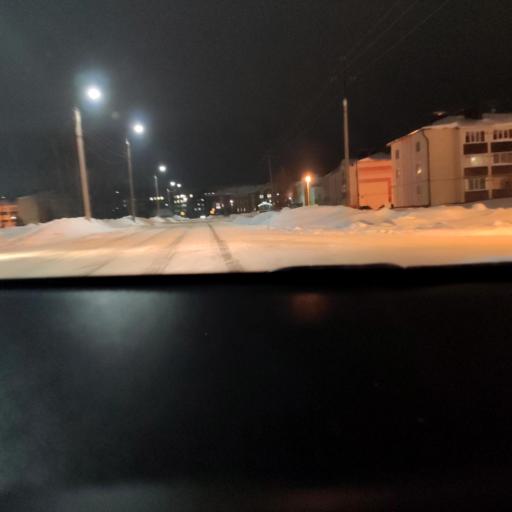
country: RU
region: Tatarstan
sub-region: Chistopol'skiy Rayon
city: Chistopol'
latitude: 55.3601
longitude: 50.5834
